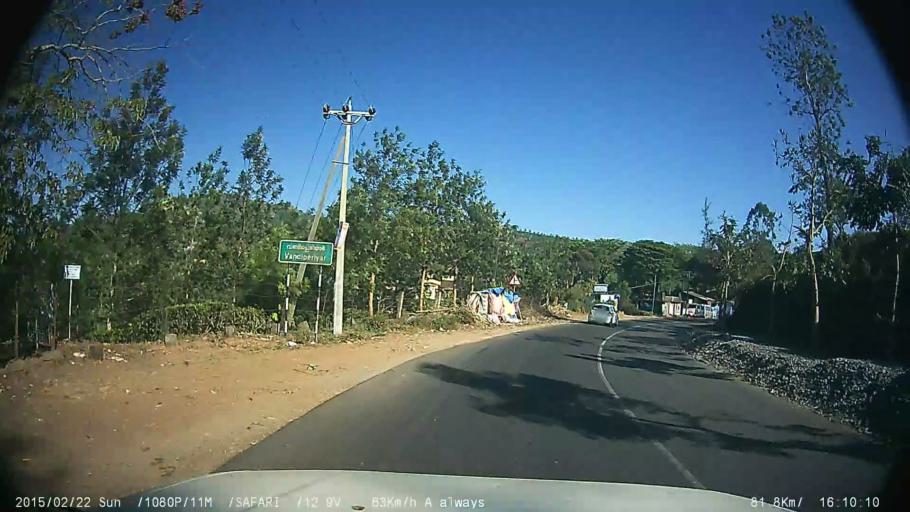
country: IN
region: Tamil Nadu
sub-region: Theni
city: Gudalur
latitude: 9.5706
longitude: 77.0852
